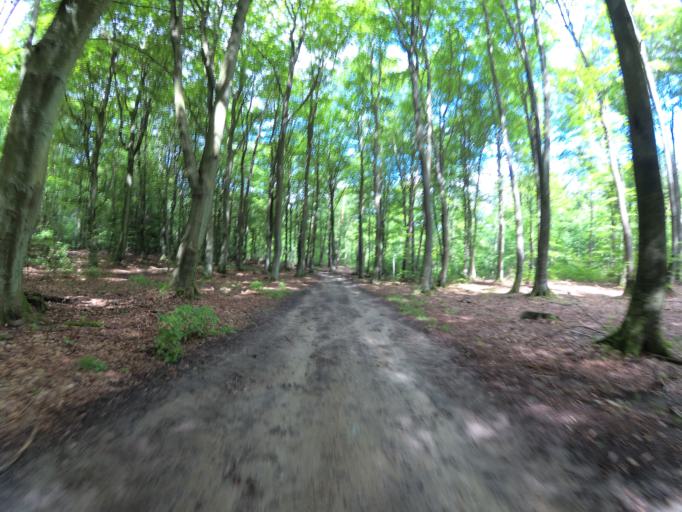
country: PL
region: Pomeranian Voivodeship
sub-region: Powiat wejherowski
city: Bojano
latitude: 54.5057
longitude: 18.4198
